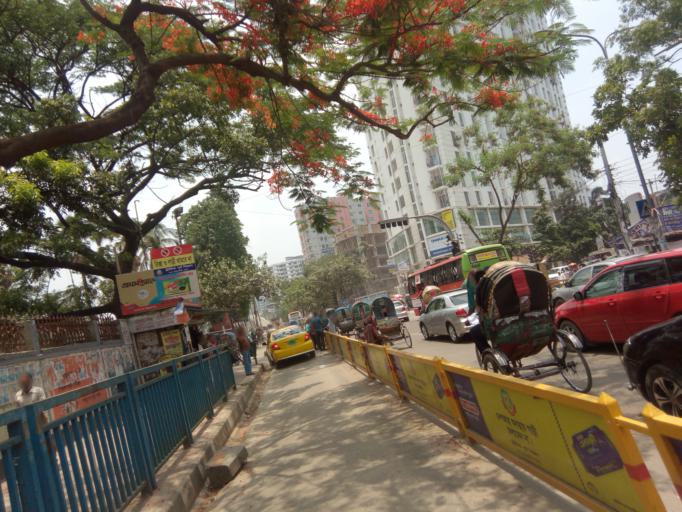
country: BD
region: Dhaka
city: Paltan
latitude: 23.7397
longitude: 90.4202
